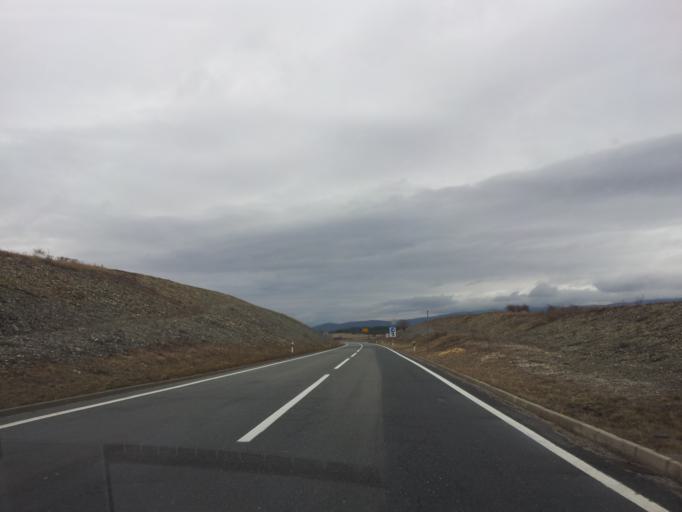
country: HR
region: Zadarska
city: Gracac
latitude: 44.5015
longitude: 15.7467
